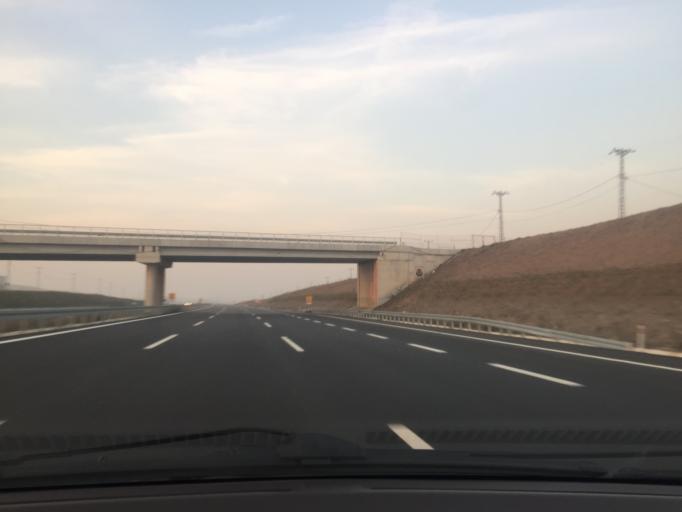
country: TR
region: Bursa
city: Karacabey
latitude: 40.2436
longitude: 28.4328
